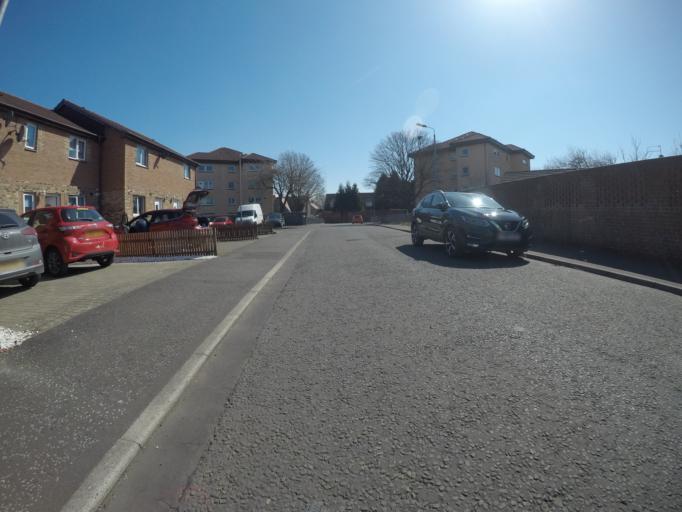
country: GB
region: Scotland
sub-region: North Ayrshire
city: Irvine
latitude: 55.6147
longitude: -4.6607
